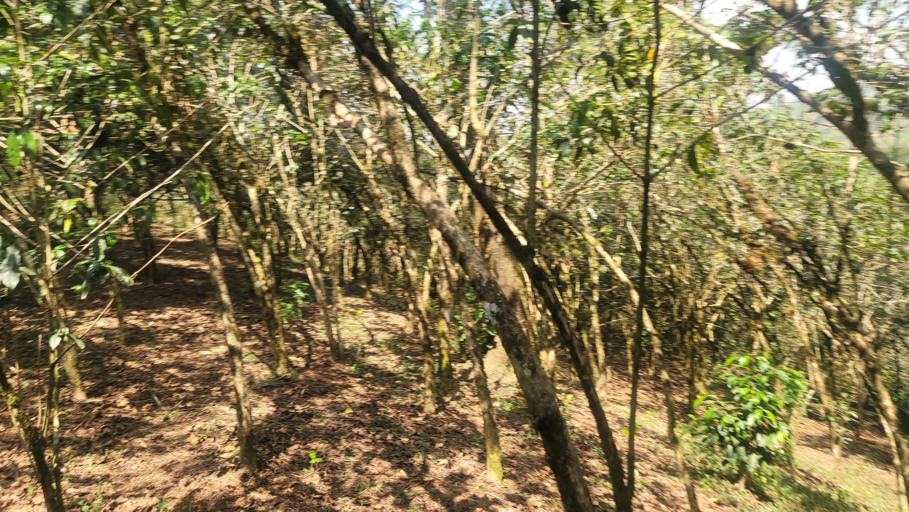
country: ET
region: Oromiya
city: Agaro
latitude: 7.7940
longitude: 36.4925
